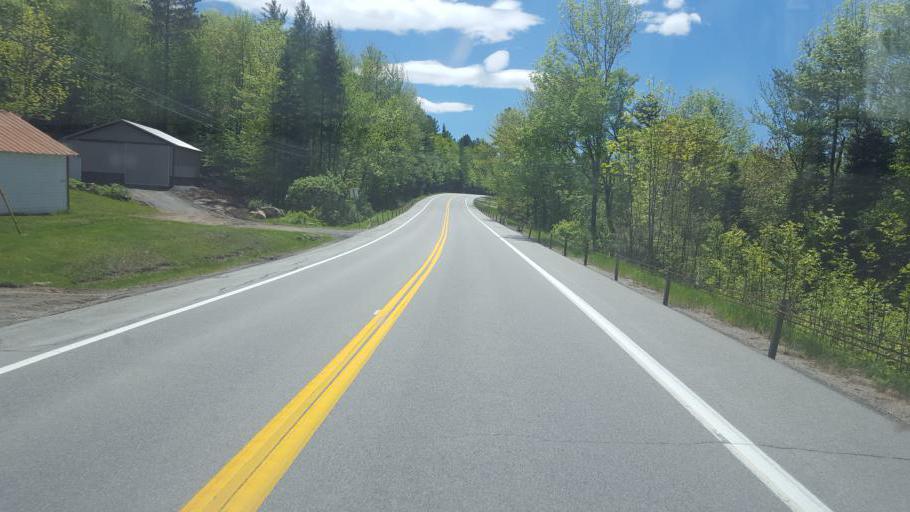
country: US
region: New York
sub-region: Hamilton County
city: Lake Pleasant
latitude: 43.4353
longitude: -74.4869
